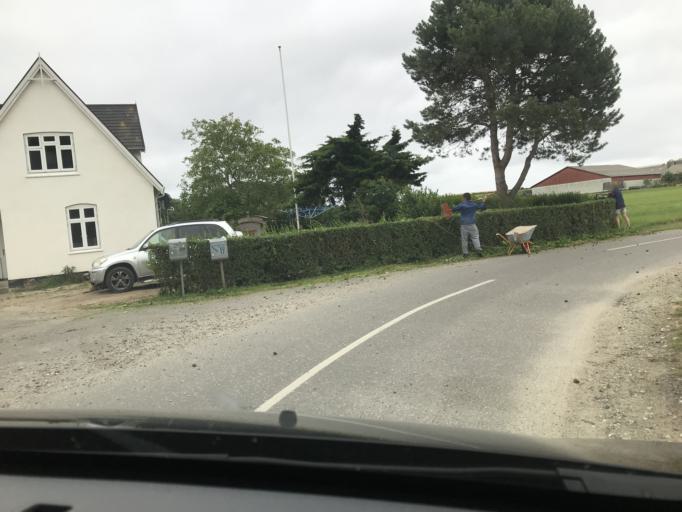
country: DK
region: South Denmark
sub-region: AEro Kommune
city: Marstal
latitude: 54.8476
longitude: 10.4778
